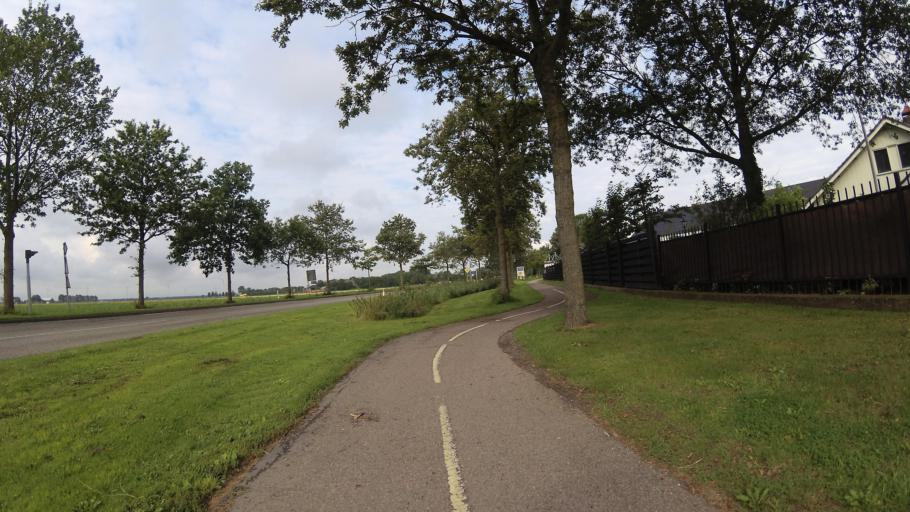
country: NL
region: North Holland
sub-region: Gemeente Hollands Kroon
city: Den Oever
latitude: 52.8447
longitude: 4.9652
